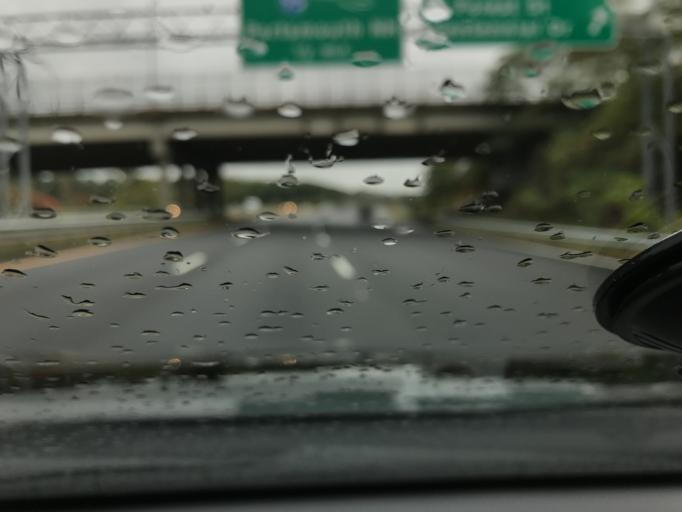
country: US
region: Massachusetts
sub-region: Essex County
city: South Peabody
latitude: 42.5275
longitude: -70.9559
